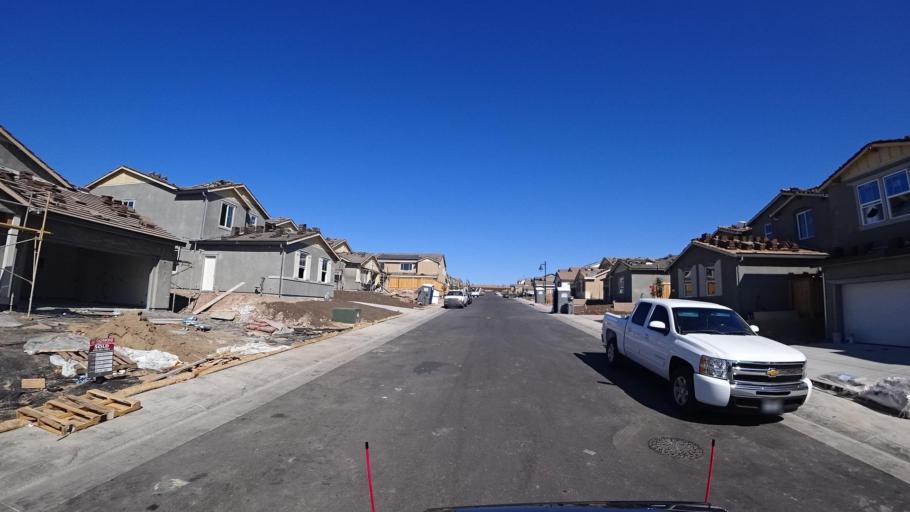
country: US
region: California
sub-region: Placer County
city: Rocklin
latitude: 38.8330
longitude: -121.2609
